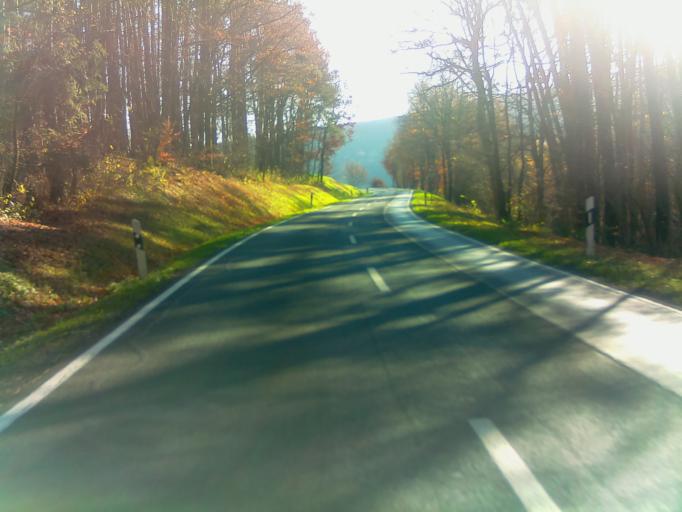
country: DE
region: Bavaria
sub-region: Regierungsbezirk Unterfranken
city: Niederlauer
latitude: 50.2944
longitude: 10.1514
